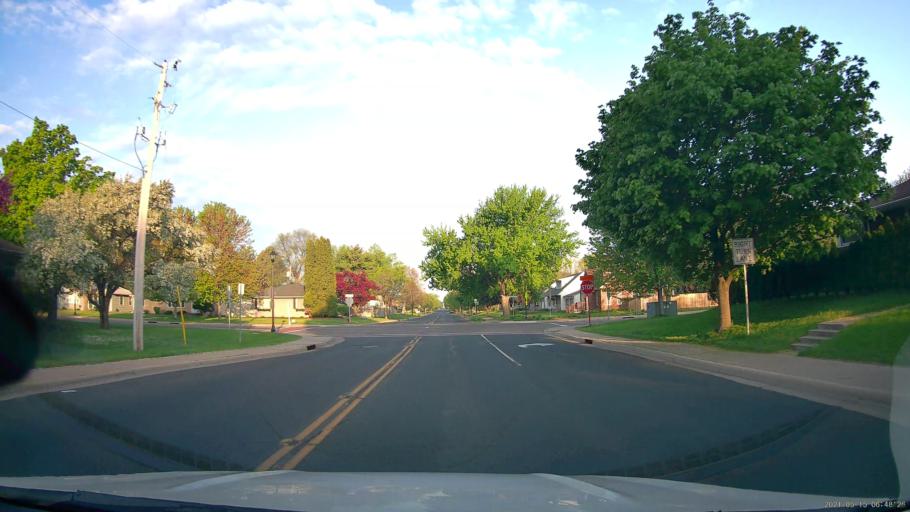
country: US
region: Minnesota
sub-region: Hennepin County
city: Saint Anthony
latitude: 45.0206
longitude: -93.2175
